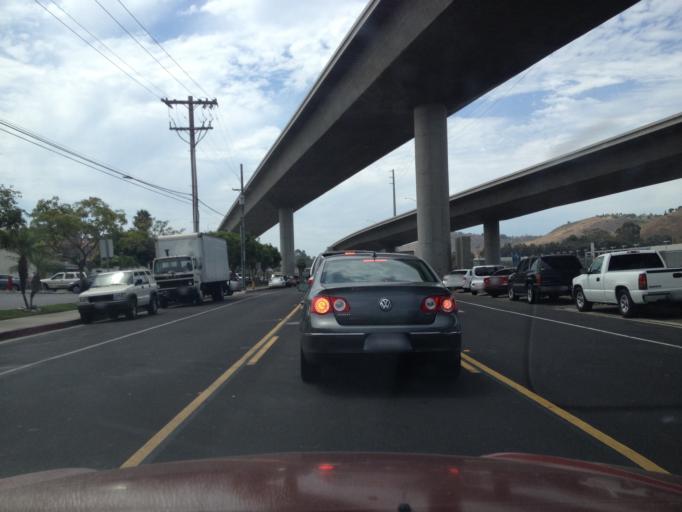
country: US
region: California
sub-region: Orange County
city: Laguna Niguel
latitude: 33.5455
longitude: -117.6742
